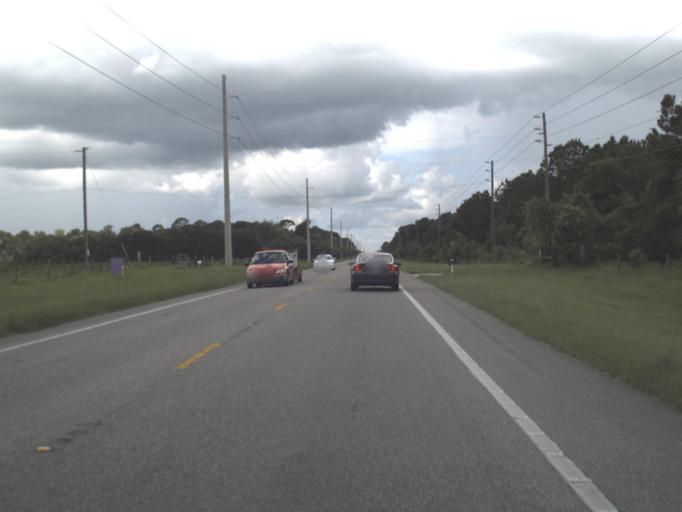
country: US
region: Florida
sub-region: Pasco County
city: Wesley Chapel
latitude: 28.3240
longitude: -82.3777
